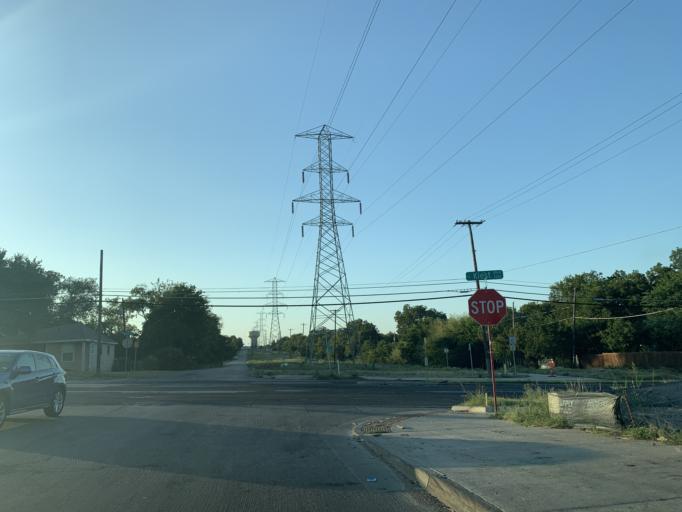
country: US
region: Texas
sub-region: Dallas County
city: Dallas
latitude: 32.7058
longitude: -96.8071
